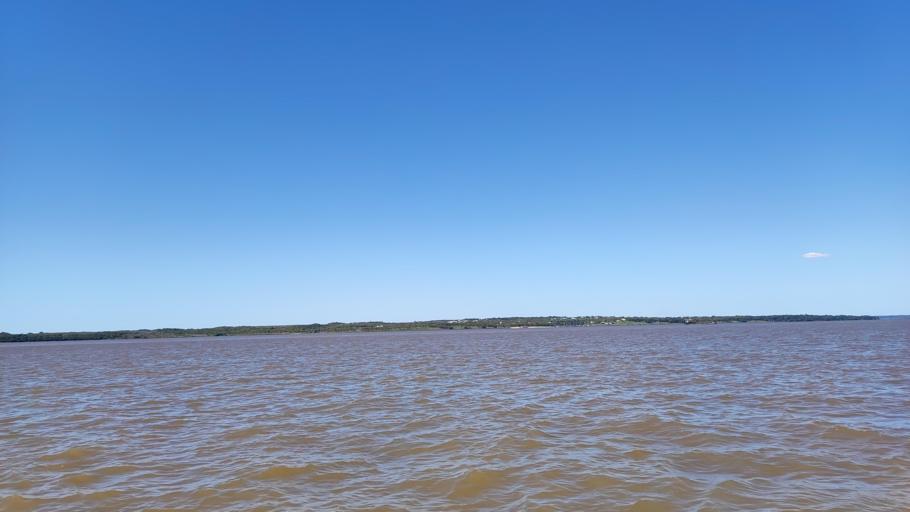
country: PY
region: Itapua
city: San Juan del Parana
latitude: -27.3392
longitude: -56.0182
